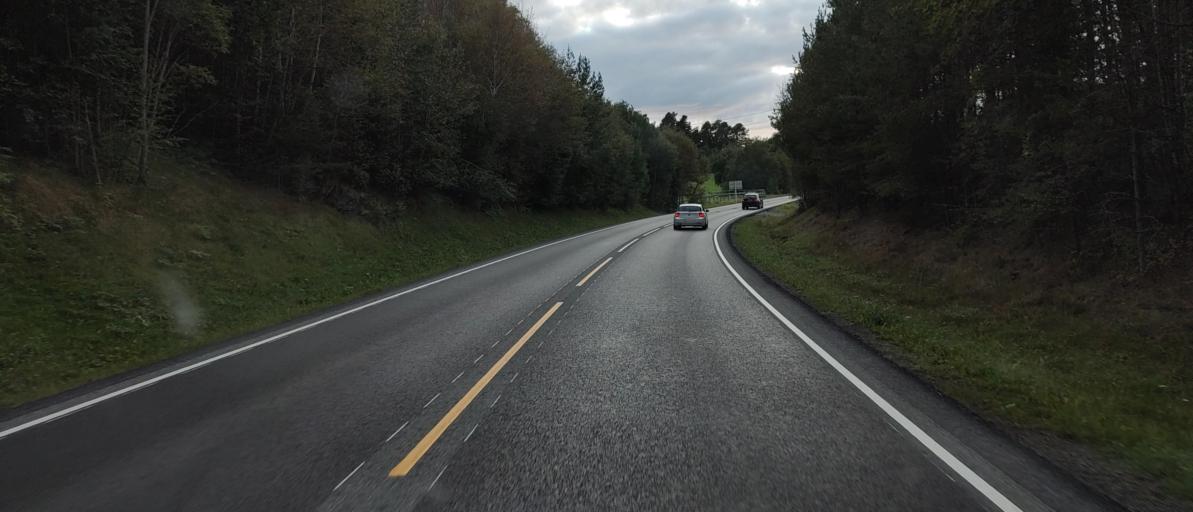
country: NO
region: More og Romsdal
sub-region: Molde
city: Molde
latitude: 62.7350
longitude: 7.3046
